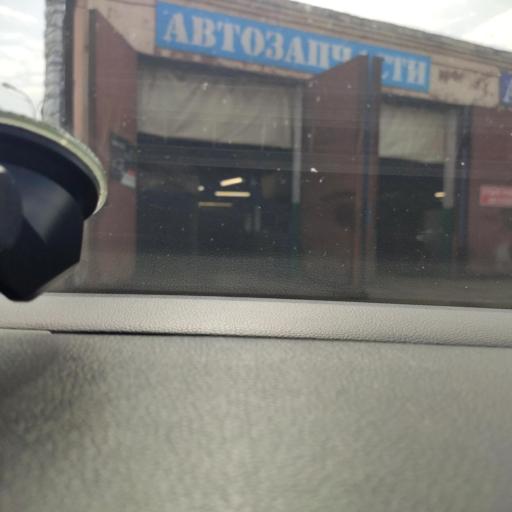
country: RU
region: Moskovskaya
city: Zvenigorod
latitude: 55.7275
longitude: 36.8666
